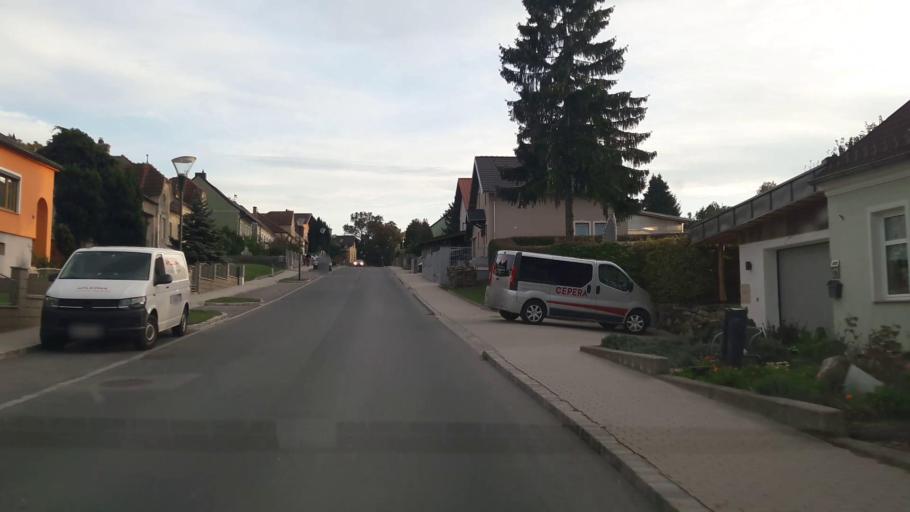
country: AT
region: Lower Austria
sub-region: Politischer Bezirk Korneuburg
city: Ernstbrunn
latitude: 48.5325
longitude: 16.3618
